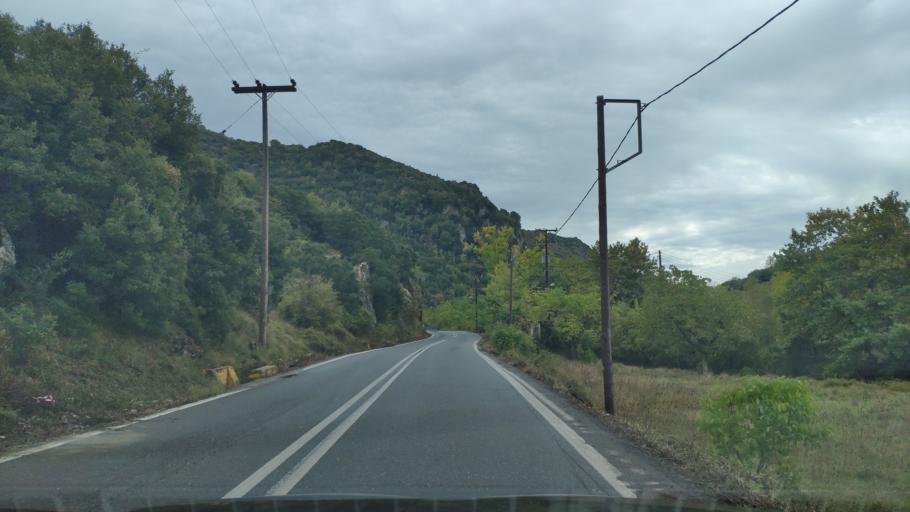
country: GR
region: Peloponnese
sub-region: Nomos Arkadias
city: Dimitsana
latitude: 37.6157
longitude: 22.0425
